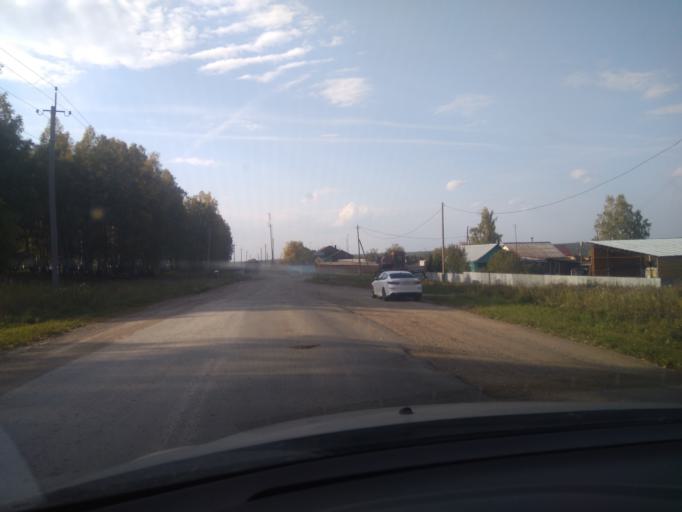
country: RU
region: Sverdlovsk
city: Pokrovskoye
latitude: 56.4305
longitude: 61.5940
